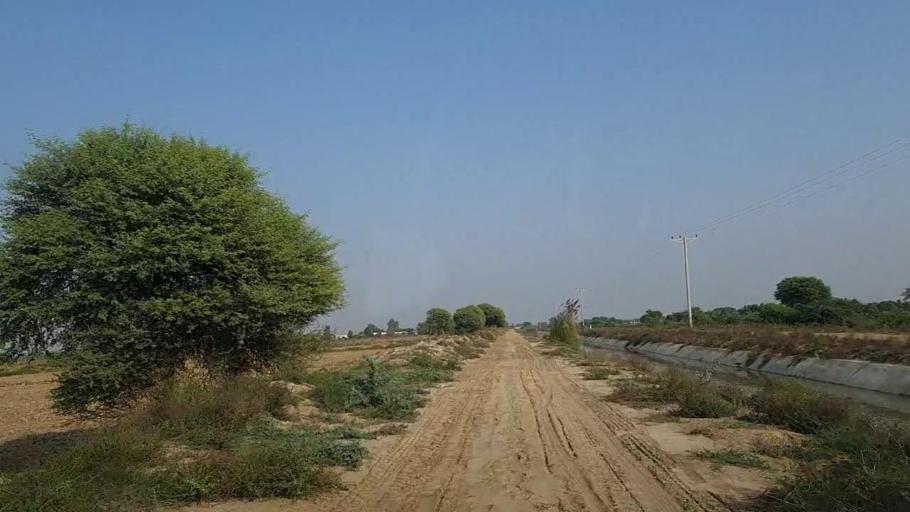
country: PK
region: Sindh
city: Mirpur Sakro
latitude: 24.6155
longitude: 67.7262
